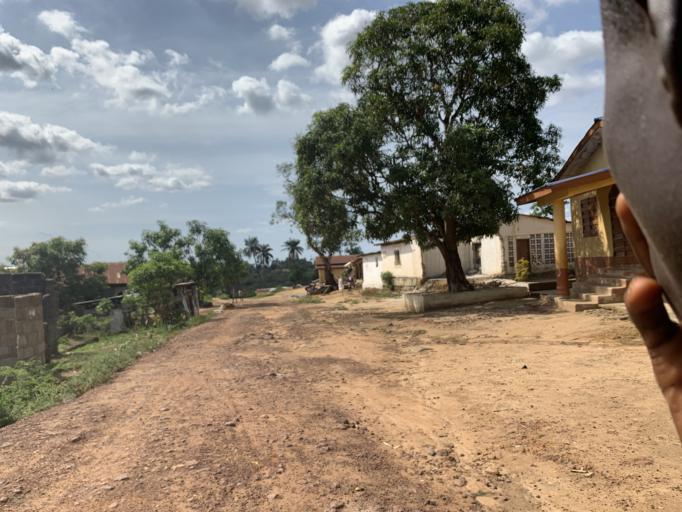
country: SL
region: Western Area
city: Waterloo
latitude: 8.3326
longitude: -13.0644
